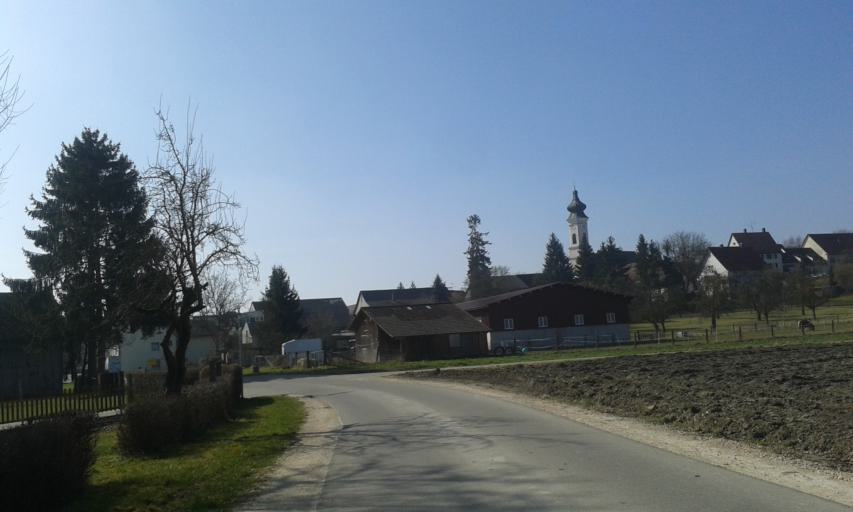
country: DE
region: Baden-Wuerttemberg
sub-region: Tuebingen Region
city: Griesingen
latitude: 48.2698
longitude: 9.7861
